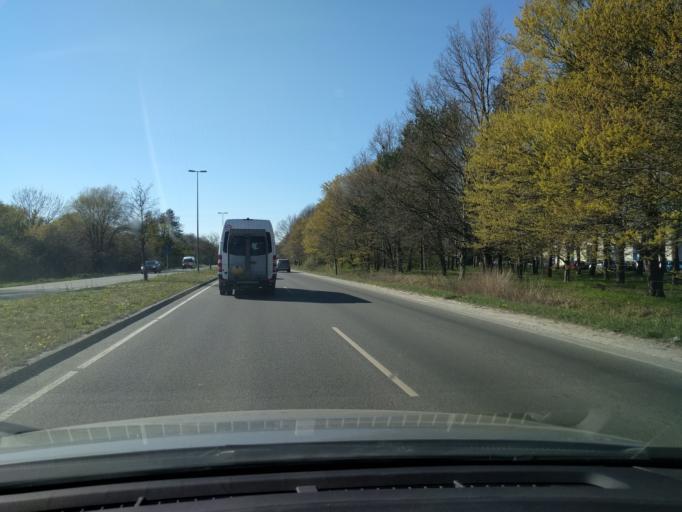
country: DK
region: Zealand
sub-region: Koge Kommune
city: Koge
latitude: 55.4812
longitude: 12.1836
